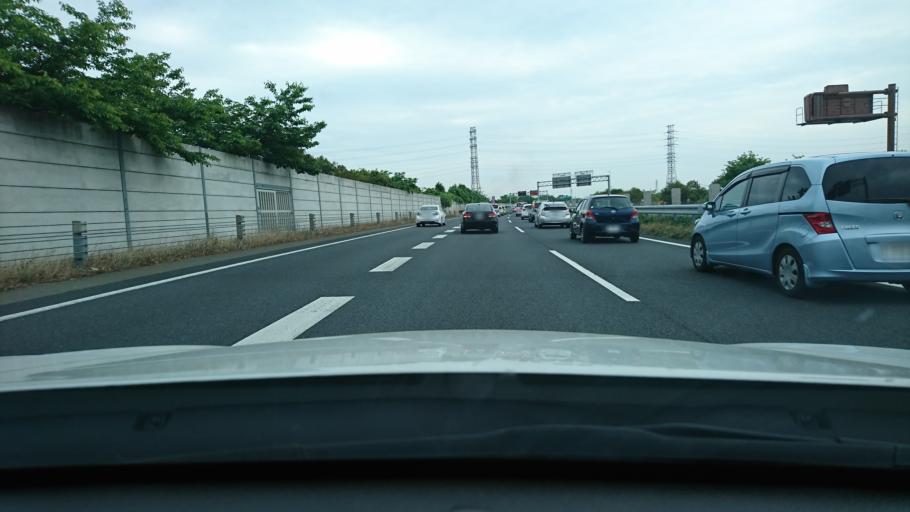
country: JP
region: Gunma
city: Fujioka
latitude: 36.2731
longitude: 139.0801
